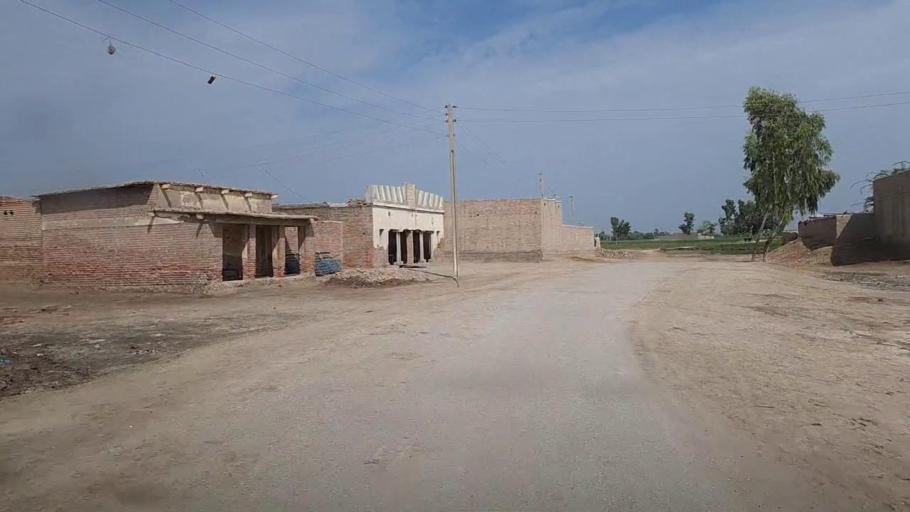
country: PK
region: Sindh
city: Thul
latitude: 28.2938
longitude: 68.8275
